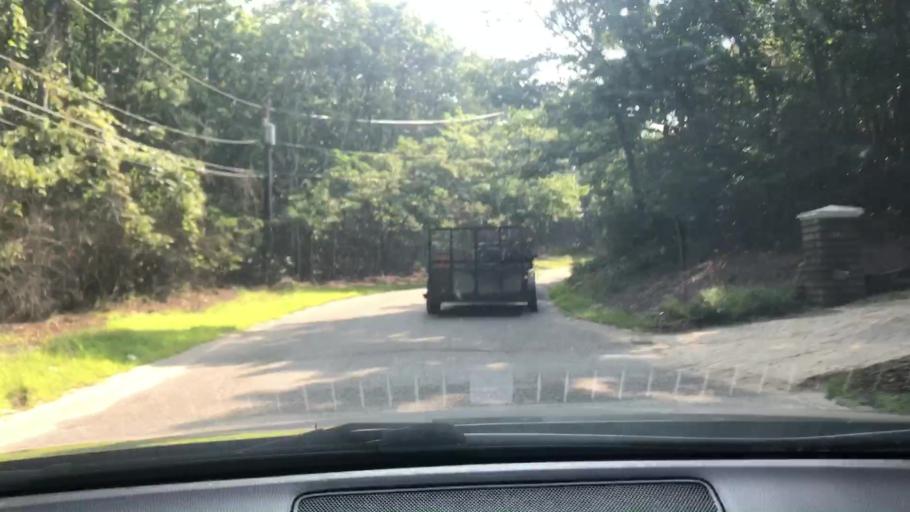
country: US
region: New York
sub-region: Suffolk County
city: Noyack
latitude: 40.9688
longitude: -72.3374
